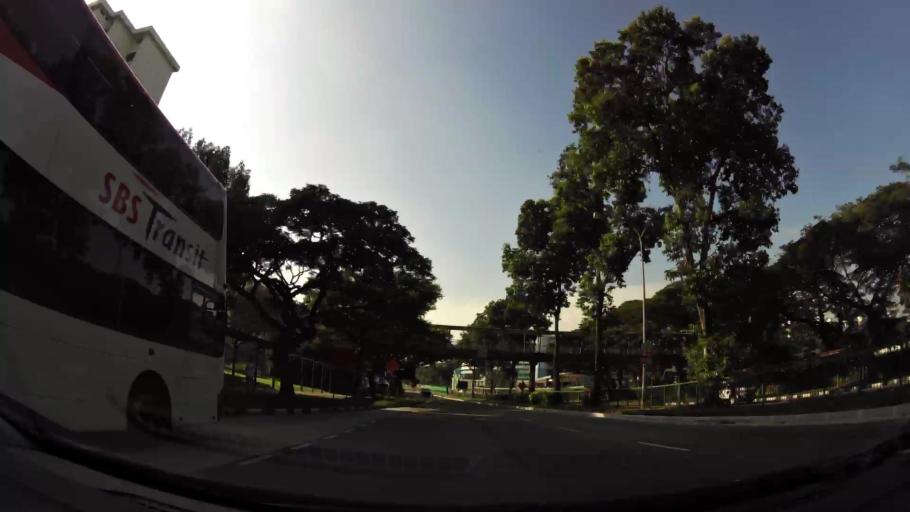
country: SG
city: Singapore
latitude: 1.3365
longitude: 103.9181
